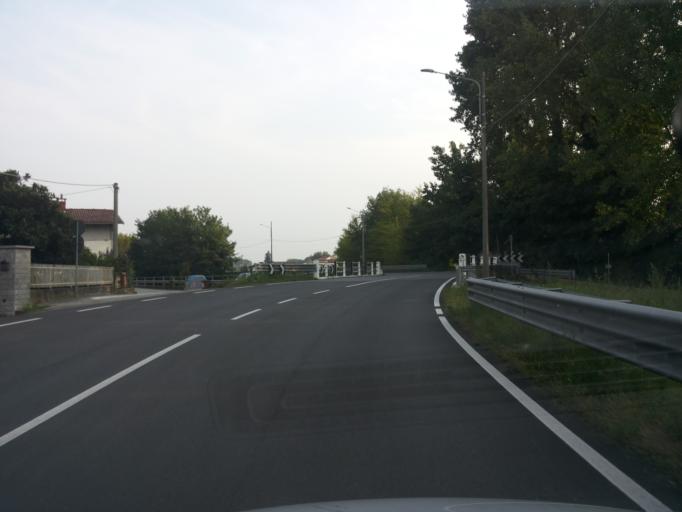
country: IT
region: Piedmont
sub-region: Provincia di Torino
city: Cascinette d'Ivrea
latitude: 45.4617
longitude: 7.9043
